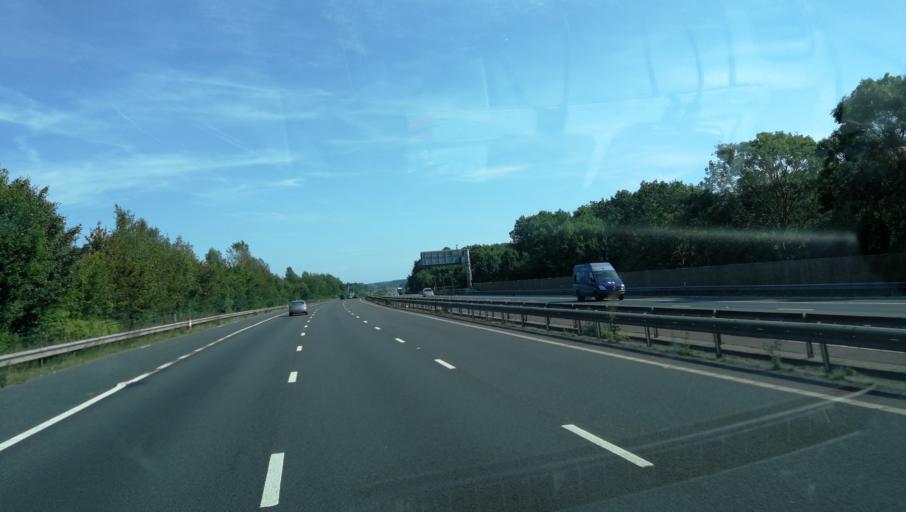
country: GB
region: England
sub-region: Kent
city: Boxley
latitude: 51.2840
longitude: 0.5794
